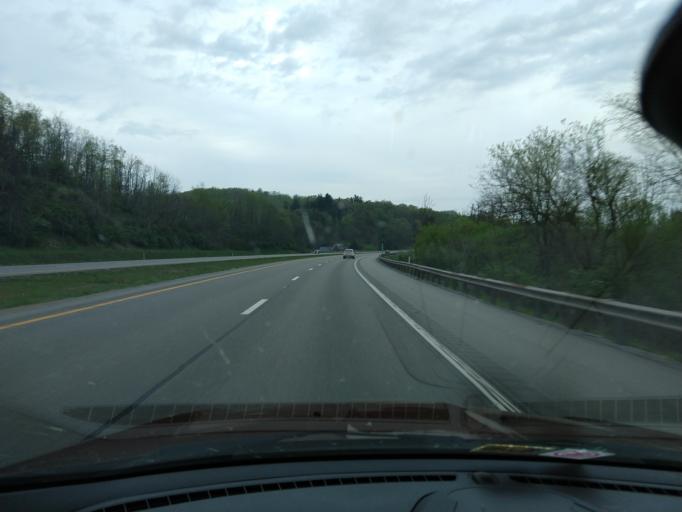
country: US
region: West Virginia
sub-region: Lewis County
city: Weston
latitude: 39.0693
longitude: -80.4048
